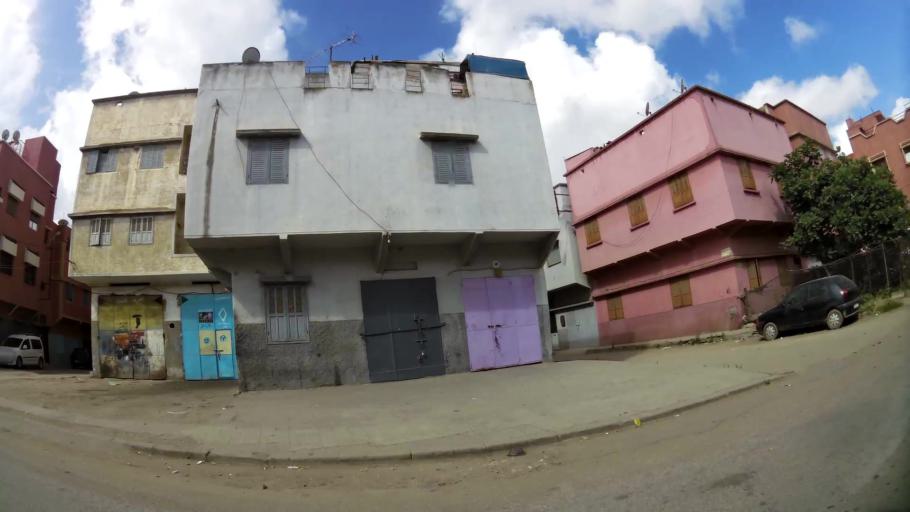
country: MA
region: Gharb-Chrarda-Beni Hssen
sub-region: Kenitra Province
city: Kenitra
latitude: 34.2704
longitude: -6.5623
